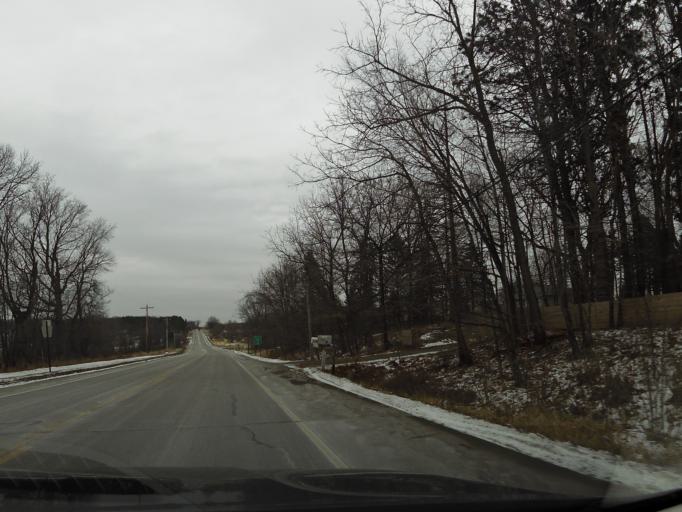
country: US
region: Minnesota
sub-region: Hennepin County
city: Orono
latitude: 44.9981
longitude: -93.5972
